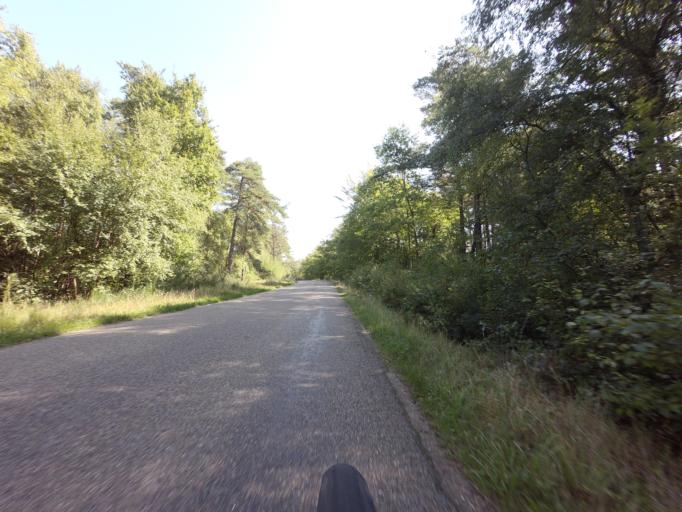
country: DK
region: North Denmark
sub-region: Hjorring Kommune
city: Hirtshals
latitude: 57.5828
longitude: 9.9980
